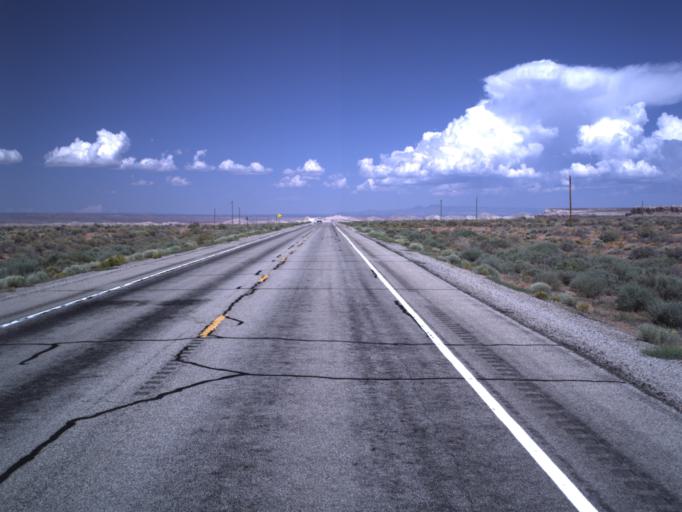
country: US
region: Utah
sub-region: San Juan County
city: Blanding
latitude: 37.1794
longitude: -109.5870
